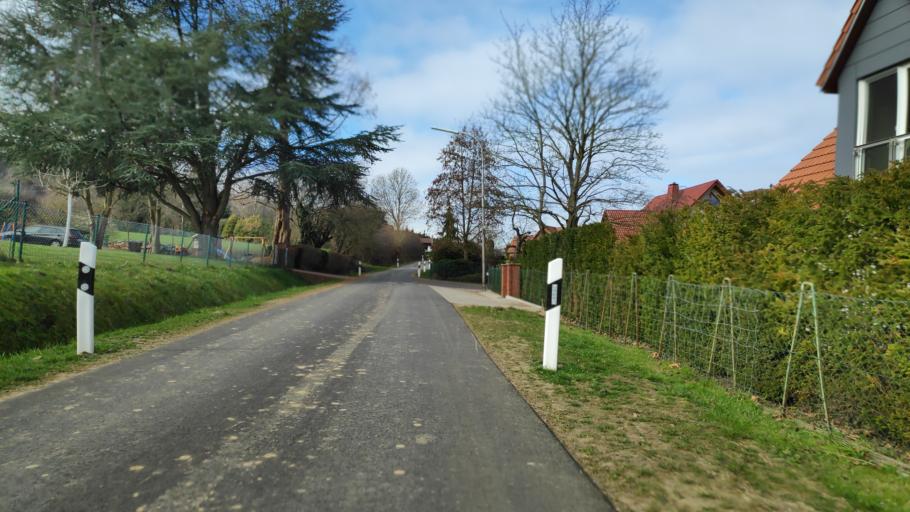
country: DE
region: North Rhine-Westphalia
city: Bad Oeynhausen
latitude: 52.2626
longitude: 8.8366
